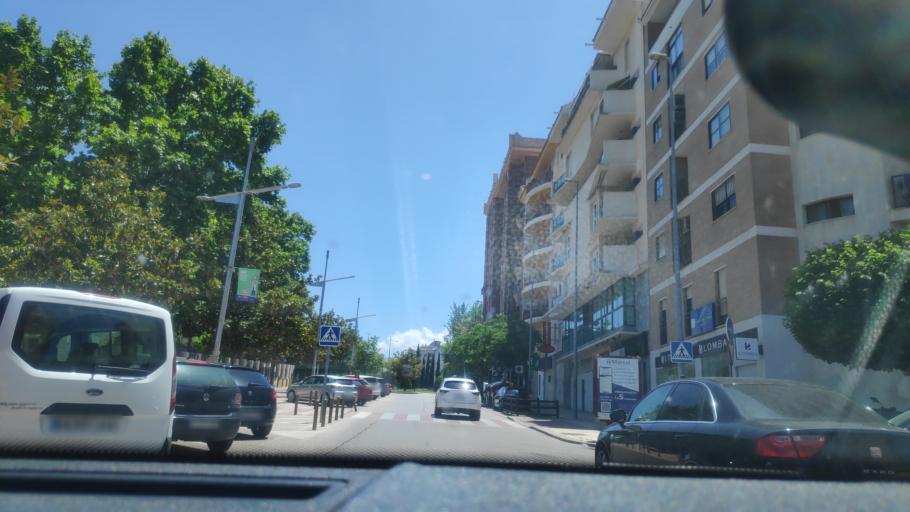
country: ES
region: Andalusia
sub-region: Provincia de Jaen
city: Jaen
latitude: 37.7818
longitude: -3.7909
